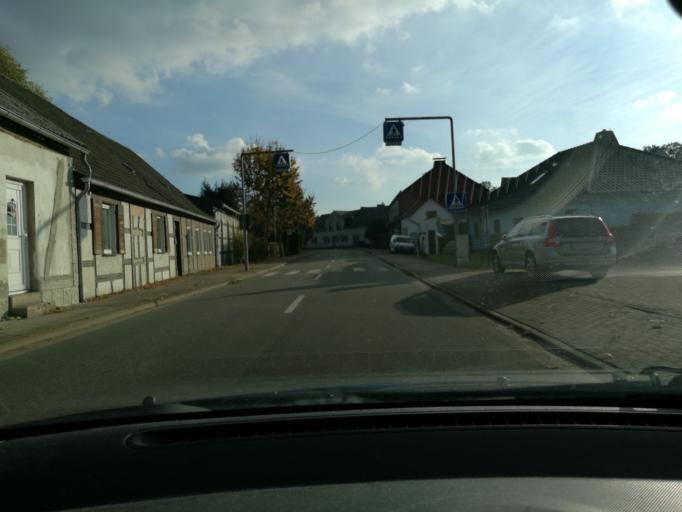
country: DE
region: Saxony-Anhalt
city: Luftkurort Arendsee
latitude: 52.8928
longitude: 11.4419
